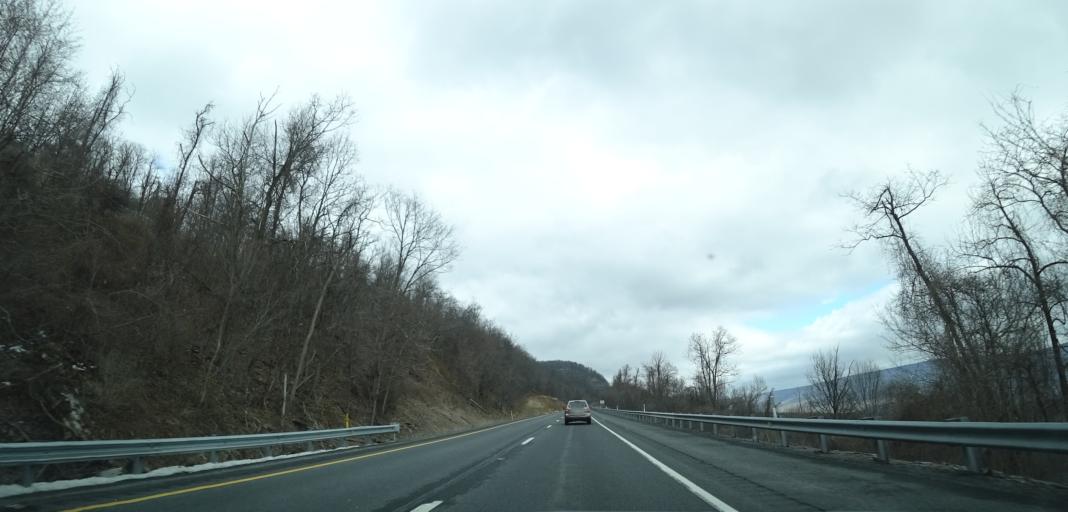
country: US
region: Pennsylvania
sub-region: Bedford County
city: Earlston
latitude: 39.8645
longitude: -78.2622
